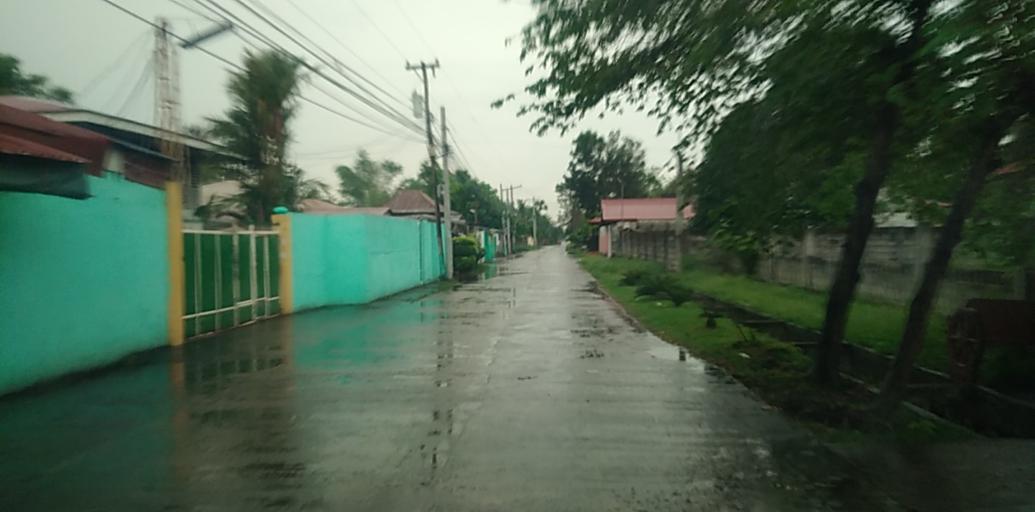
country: PH
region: Central Luzon
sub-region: Province of Pampanga
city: Arenas
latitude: 15.1671
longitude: 120.6878
